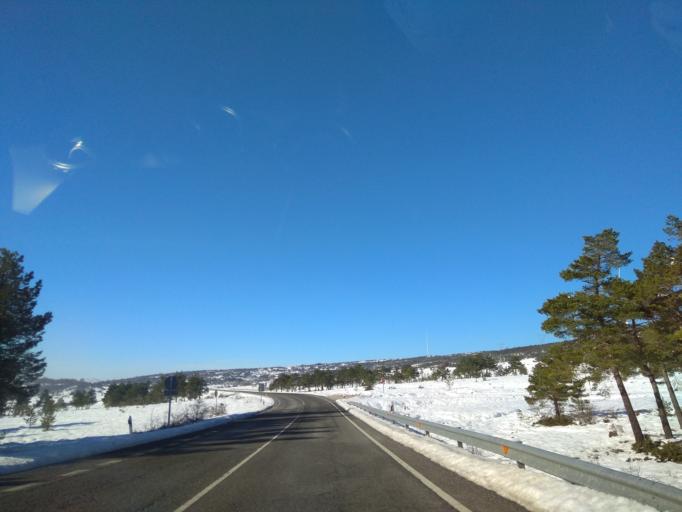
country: ES
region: Castille and Leon
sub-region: Provincia de Burgos
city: Espinosa de los Monteros
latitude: 42.9424
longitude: -3.6779
